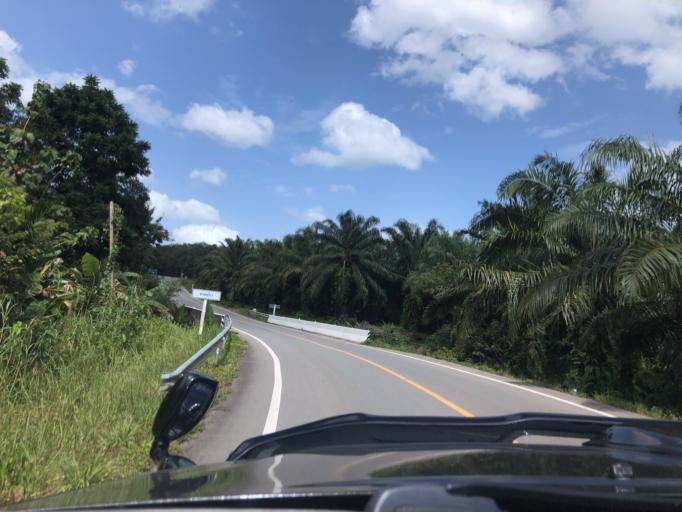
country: TH
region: Krabi
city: Khlong Thom
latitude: 7.9463
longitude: 99.2101
